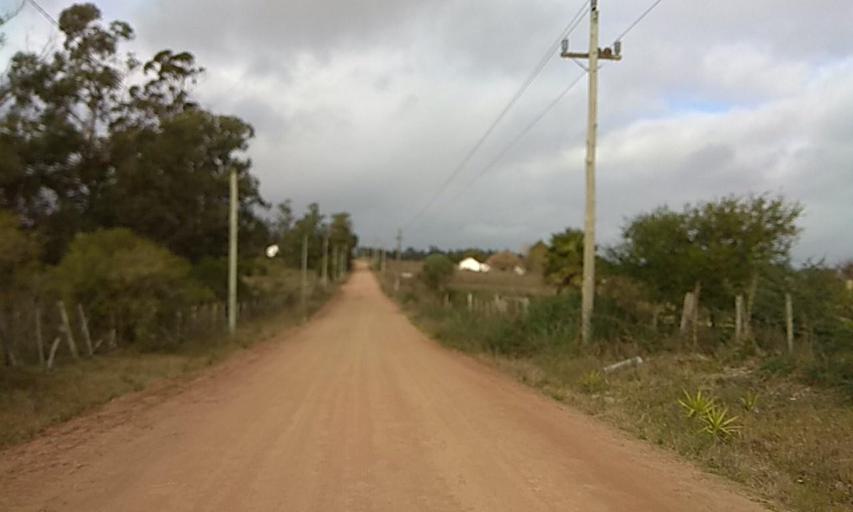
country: UY
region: Florida
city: Florida
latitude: -34.0663
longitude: -56.2188
